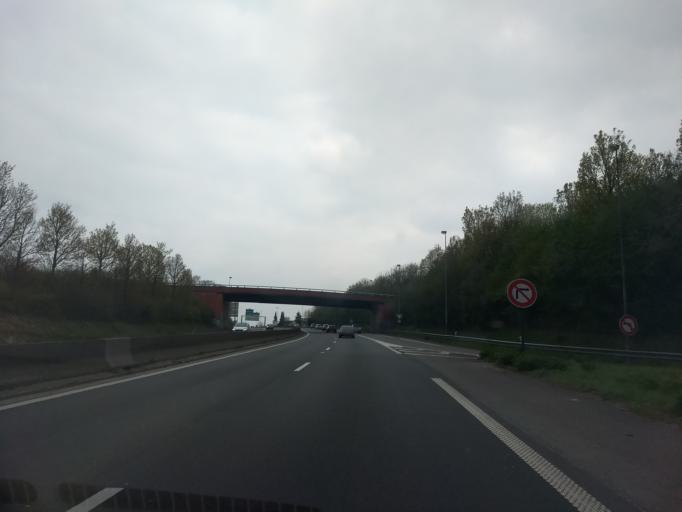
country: FR
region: Nord-Pas-de-Calais
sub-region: Departement du Pas-de-Calais
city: Saint-Nicolas
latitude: 50.3117
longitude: 2.7767
